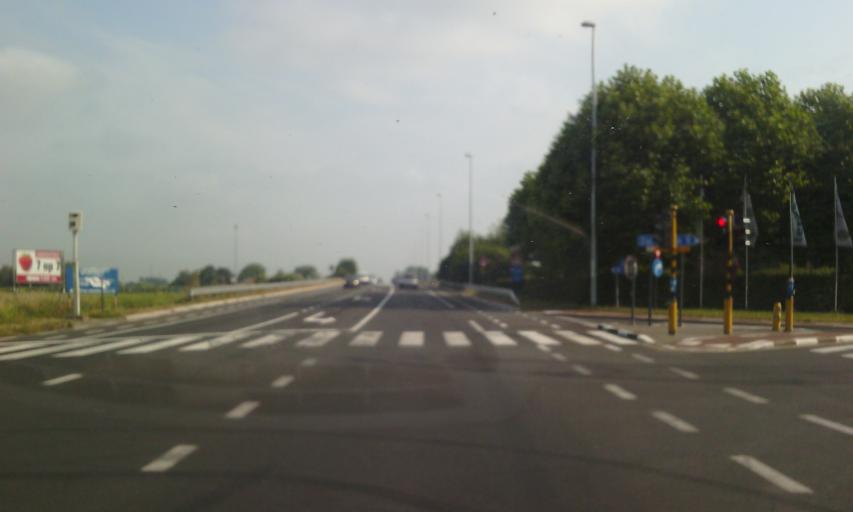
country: BE
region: Flanders
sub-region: Provincie Oost-Vlaanderen
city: Waarschoot
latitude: 51.1401
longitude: 3.6026
